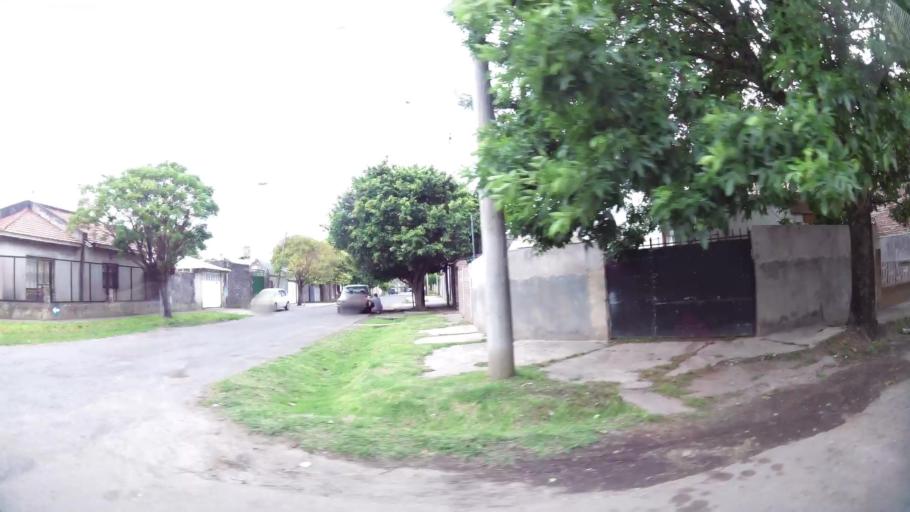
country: AR
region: Santa Fe
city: Gobernador Galvez
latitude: -32.9982
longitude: -60.6622
